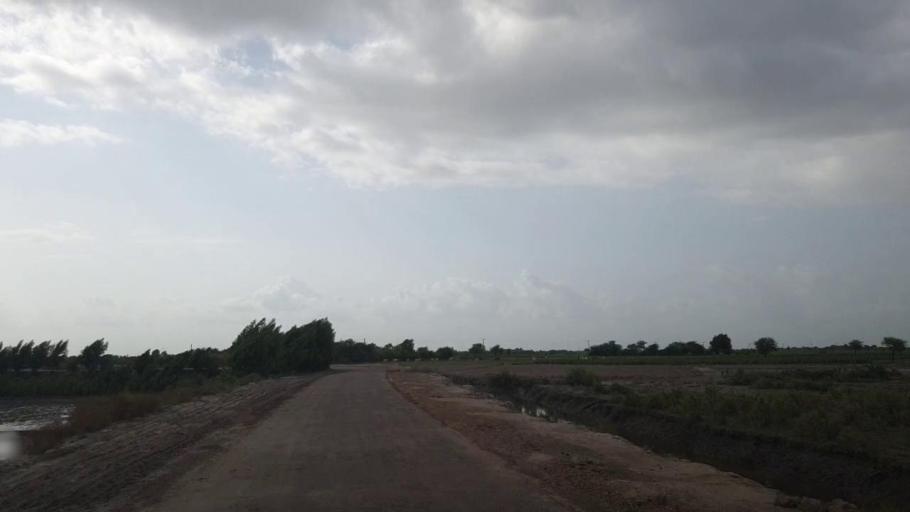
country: PK
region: Sindh
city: Kadhan
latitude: 24.5852
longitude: 69.0566
